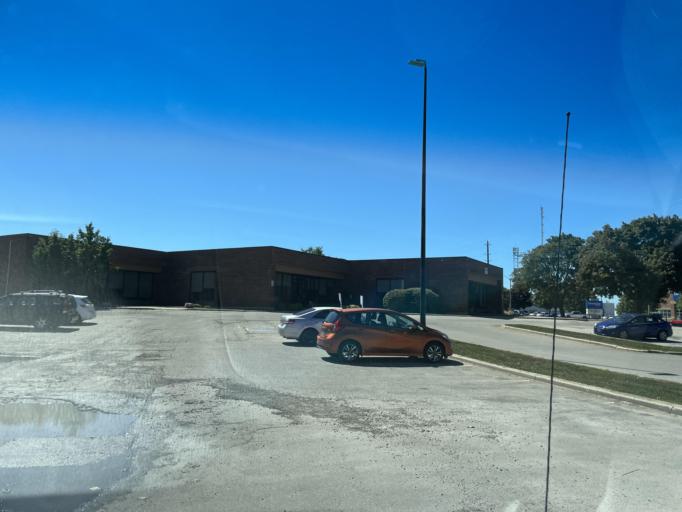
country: CA
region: Ontario
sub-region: Wellington County
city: Guelph
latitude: 43.5422
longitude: -80.3076
